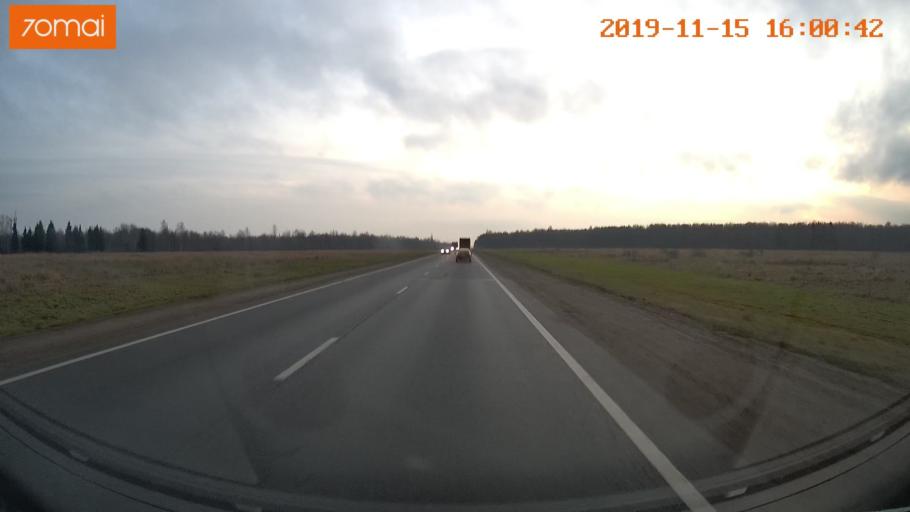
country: RU
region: Jaroslavl
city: Yaroslavl
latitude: 57.7929
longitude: 39.9371
